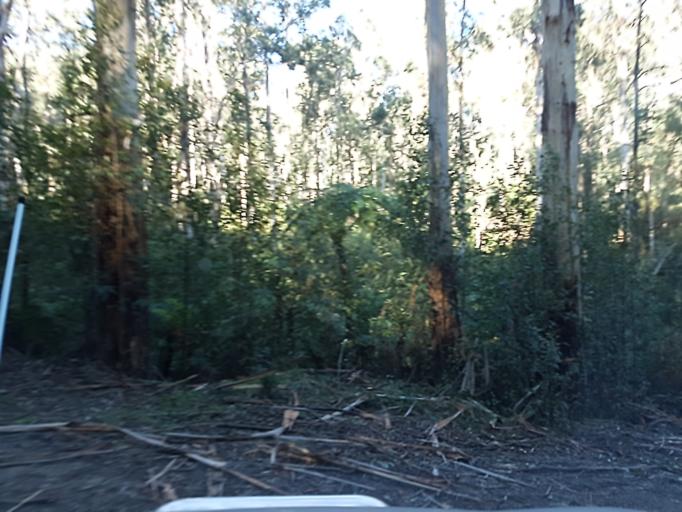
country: AU
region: Victoria
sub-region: Yarra Ranges
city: Healesville
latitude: -37.5797
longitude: 145.4896
